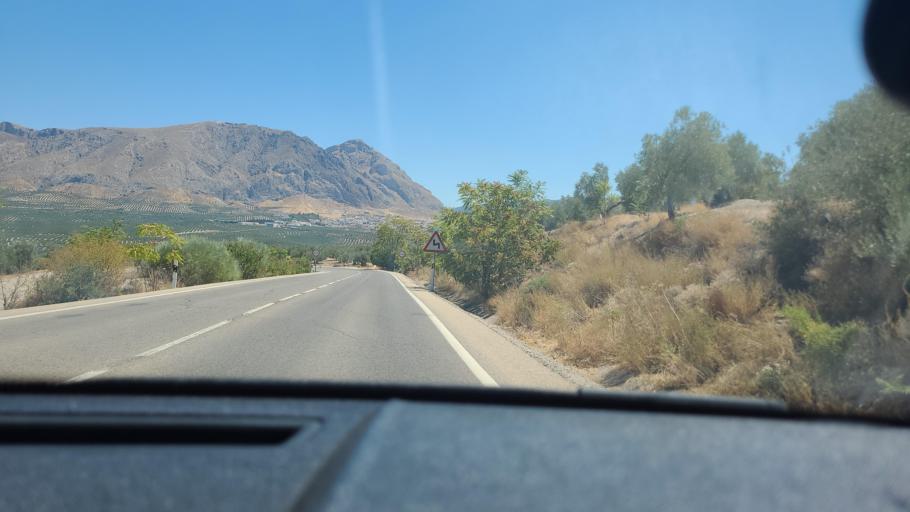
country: ES
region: Andalusia
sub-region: Provincia de Jaen
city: Jimena
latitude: 37.8368
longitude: -3.4513
